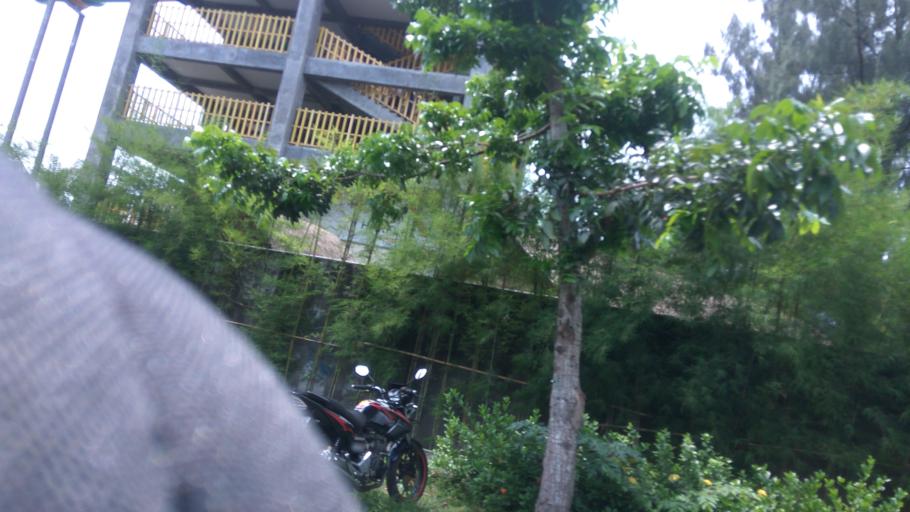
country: ID
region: Daerah Istimewa Yogyakarta
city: Depok
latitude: -7.7463
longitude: 110.4183
